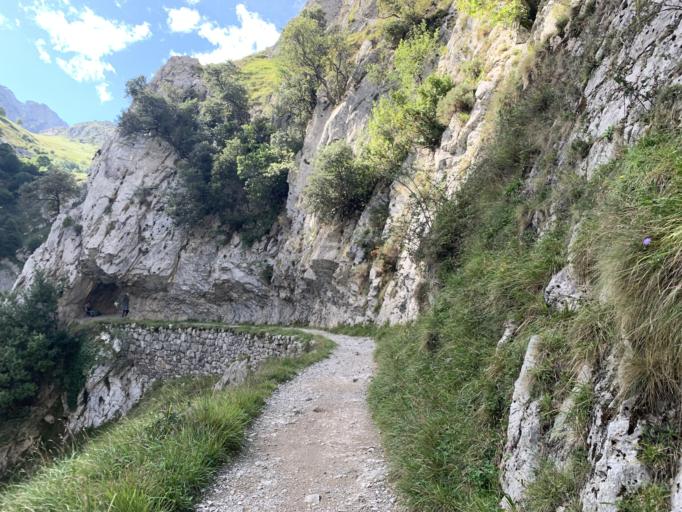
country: ES
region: Asturias
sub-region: Province of Asturias
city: Carrena
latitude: 43.2448
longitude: -4.8877
